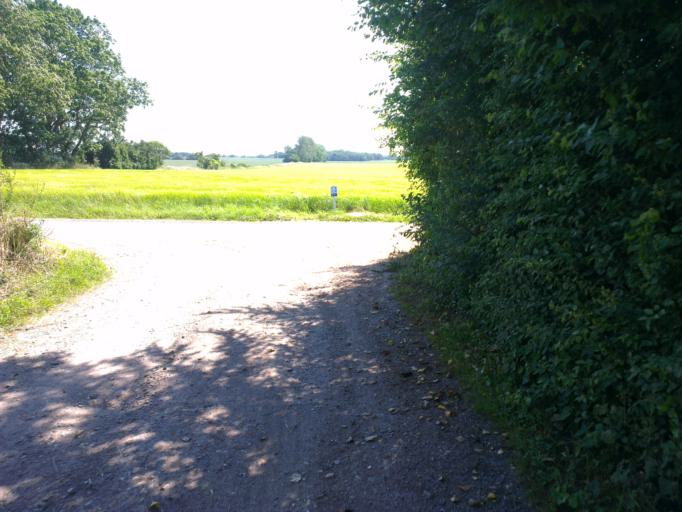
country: DK
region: Capital Region
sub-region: Frederikssund Kommune
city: Jaegerspris
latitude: 55.8134
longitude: 11.9517
